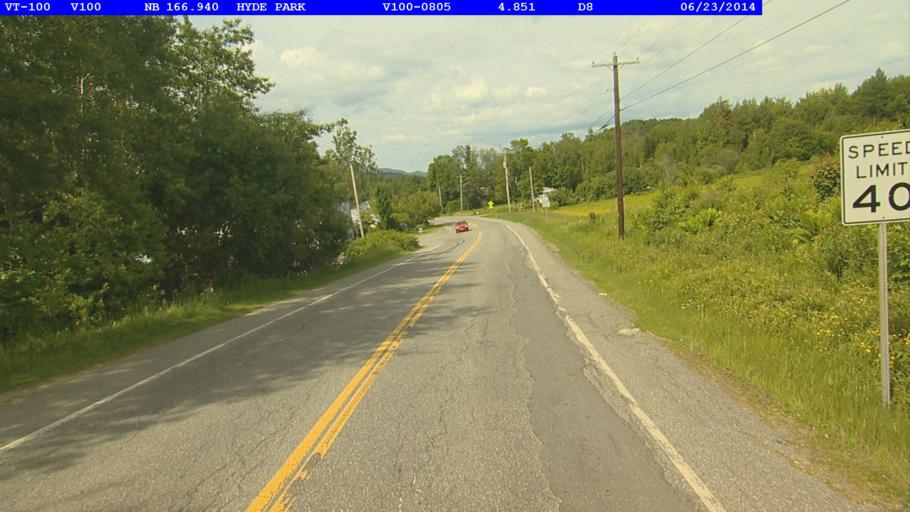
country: US
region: Vermont
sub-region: Lamoille County
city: Hyde Park
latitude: 44.6629
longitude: -72.6062
